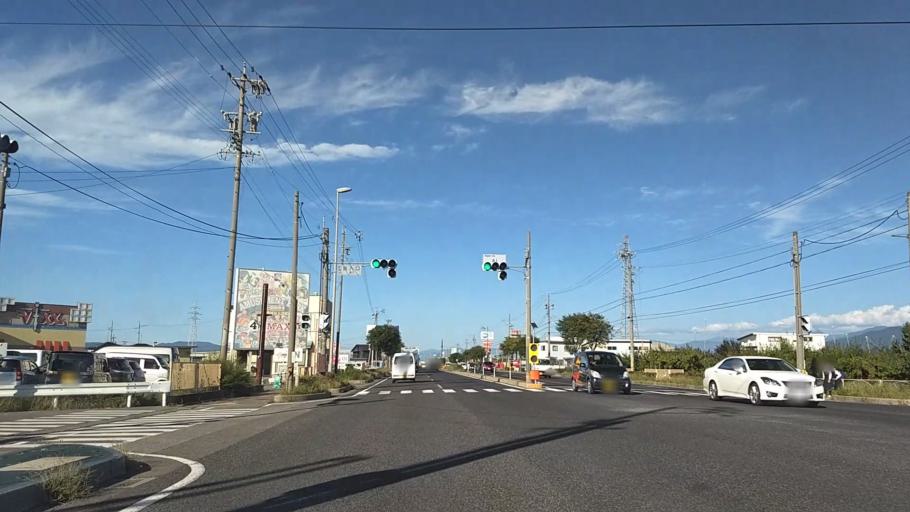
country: JP
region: Nagano
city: Nagano-shi
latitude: 36.5692
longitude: 138.1502
